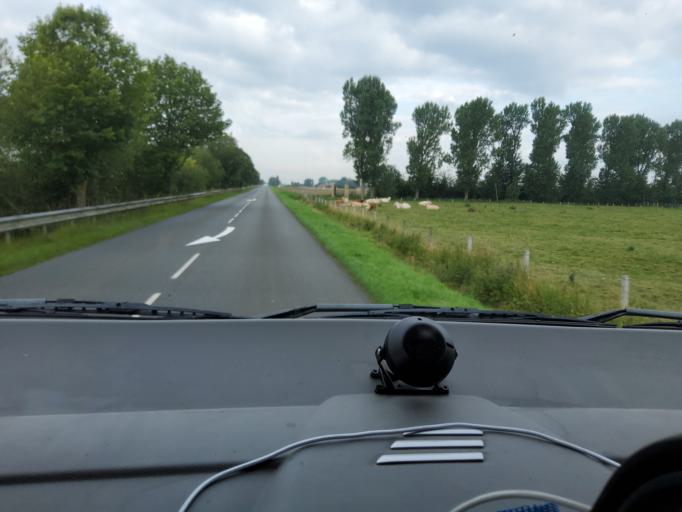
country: FR
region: Nord-Pas-de-Calais
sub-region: Departement du Nord
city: Bierne
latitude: 50.9704
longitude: 2.3928
